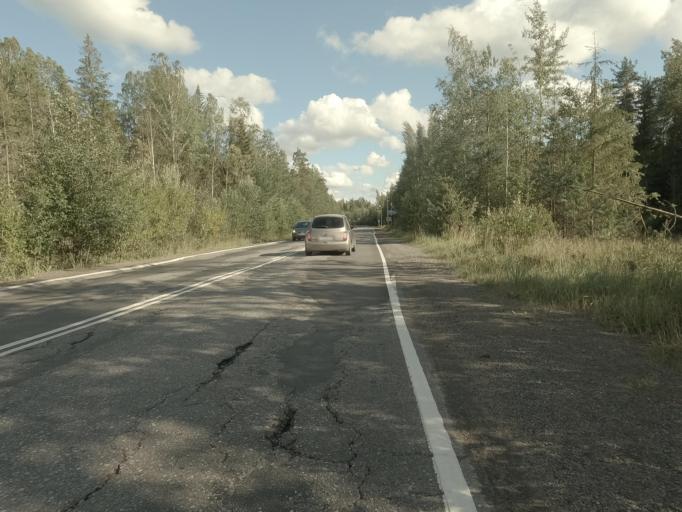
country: RU
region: Leningrad
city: Borisova Griva
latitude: 59.9877
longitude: 30.8875
